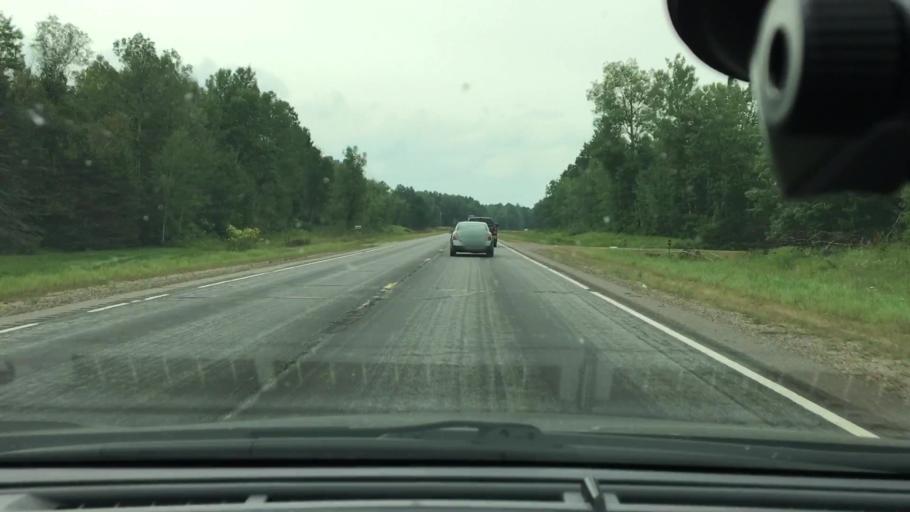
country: US
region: Minnesota
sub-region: Crow Wing County
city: Cross Lake
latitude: 46.6740
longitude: -93.9521
